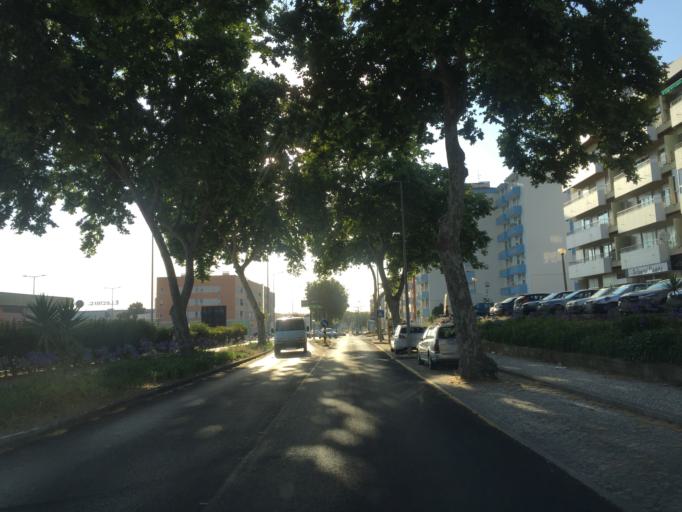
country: PT
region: Leiria
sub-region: Caldas da Rainha
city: Caldas da Rainha
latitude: 39.4031
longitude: -9.1432
